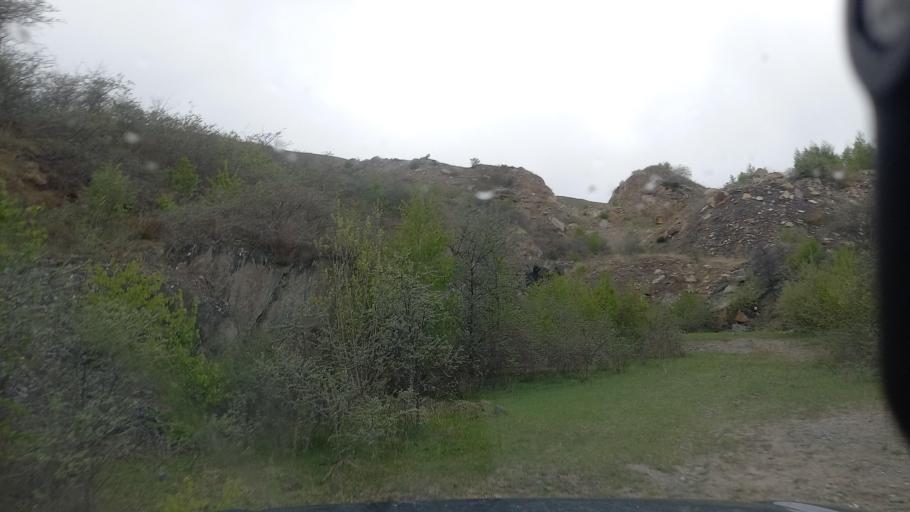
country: RU
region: Kabardino-Balkariya
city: Bylym
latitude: 43.4573
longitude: 42.9973
